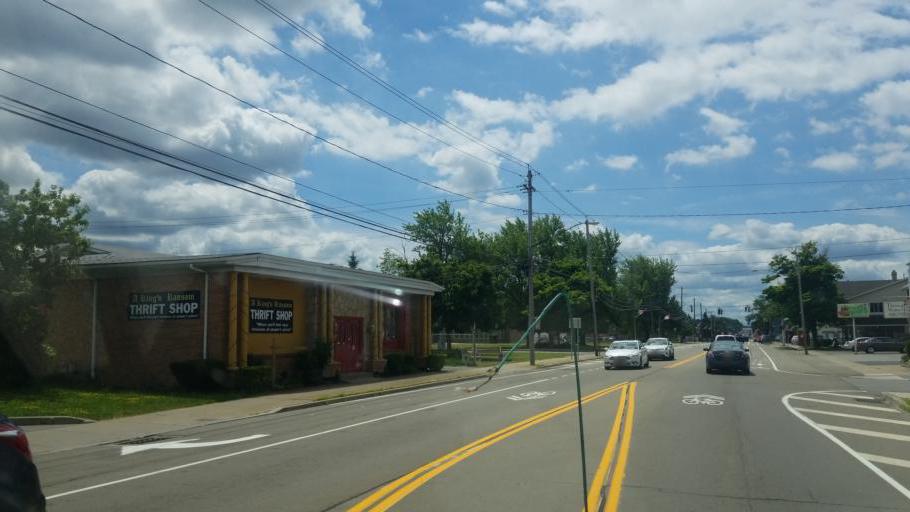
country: US
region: New York
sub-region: Erie County
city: Blasdell
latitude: 42.7967
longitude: -78.8239
